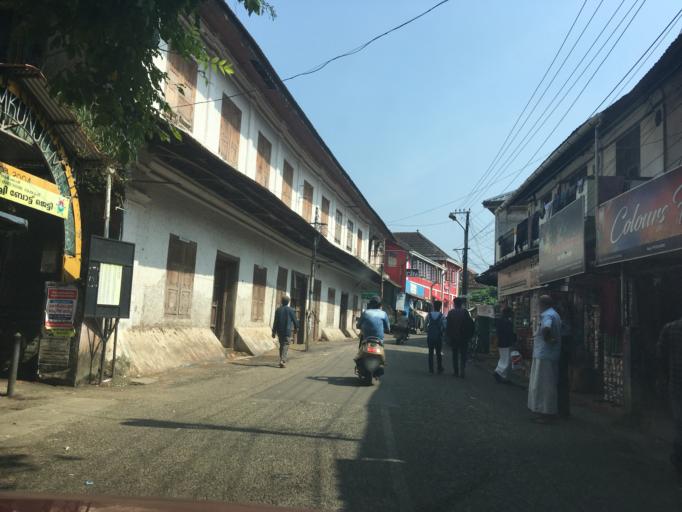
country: IN
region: Kerala
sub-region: Ernakulam
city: Cochin
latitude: 9.9687
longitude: 76.2515
